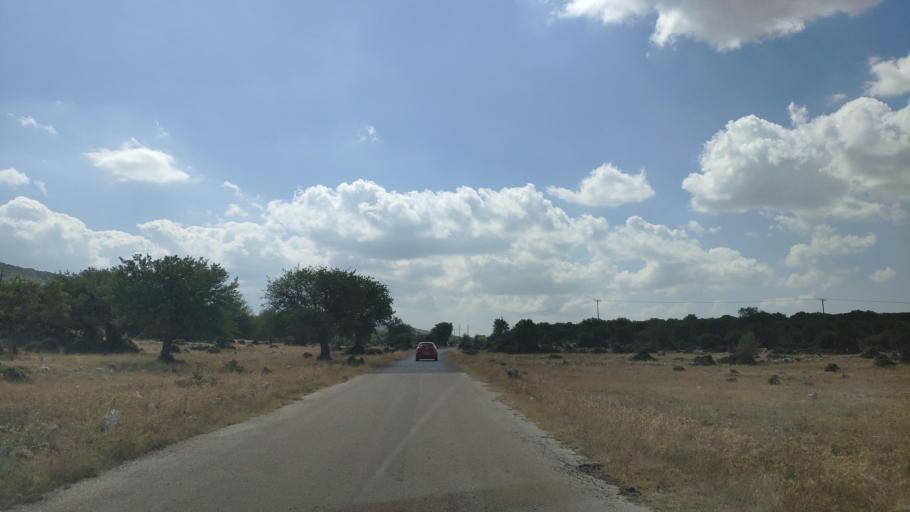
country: GR
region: Peloponnese
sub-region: Nomos Lakonias
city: Kariai
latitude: 37.3098
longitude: 22.4530
